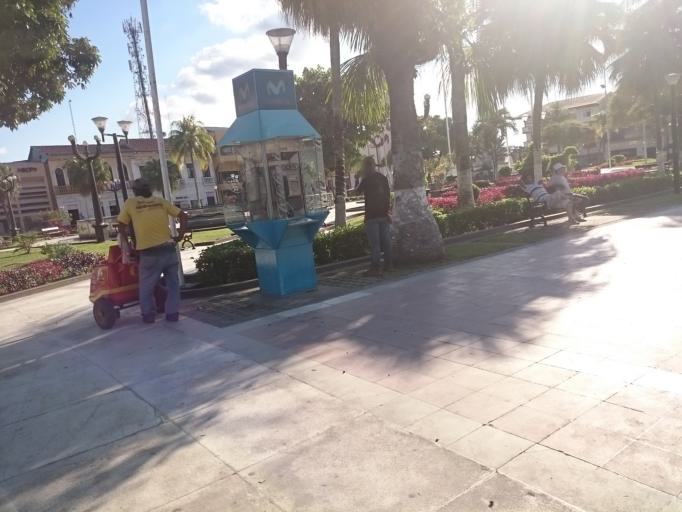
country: PE
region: Loreto
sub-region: Provincia de Maynas
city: Iquitos
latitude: -3.7494
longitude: -73.2439
